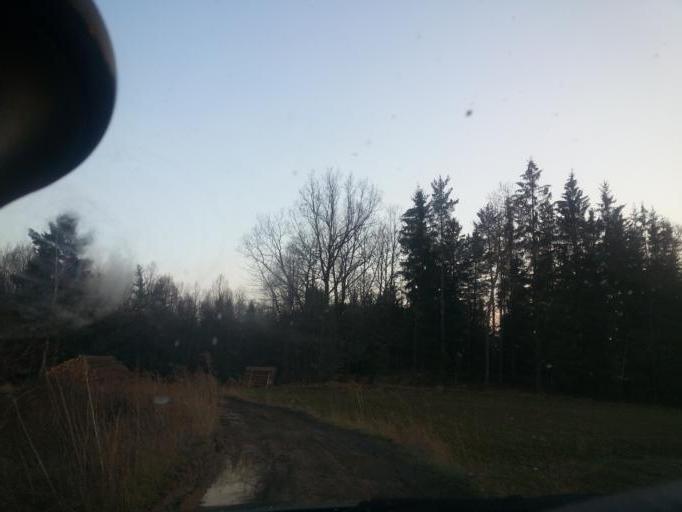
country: PL
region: Lower Silesian Voivodeship
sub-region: Powiat jeleniogorski
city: Stara Kamienica
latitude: 50.9534
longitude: 15.6227
